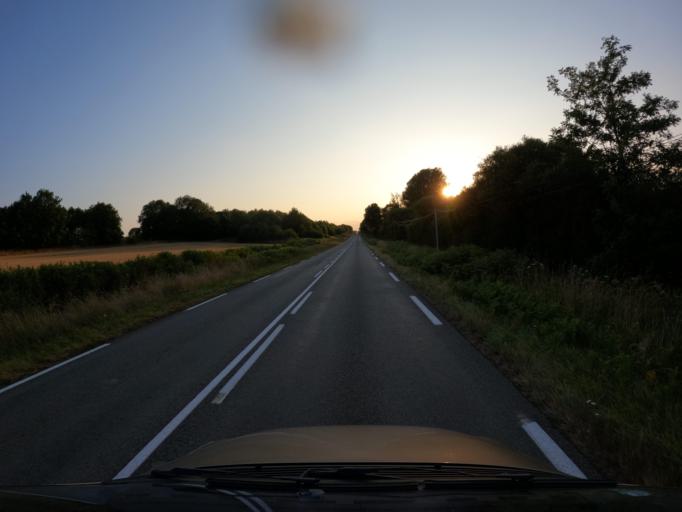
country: FR
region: Pays de la Loire
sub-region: Departement de la Sarthe
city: Auvers-le-Hamon
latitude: 47.8679
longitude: -0.4353
